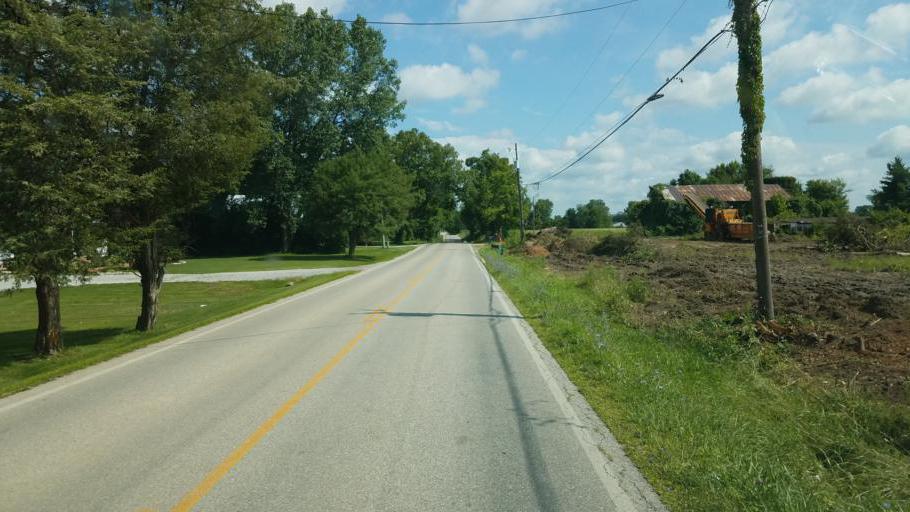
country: US
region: Ohio
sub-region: Delaware County
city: Sunbury
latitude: 40.2695
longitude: -82.9386
